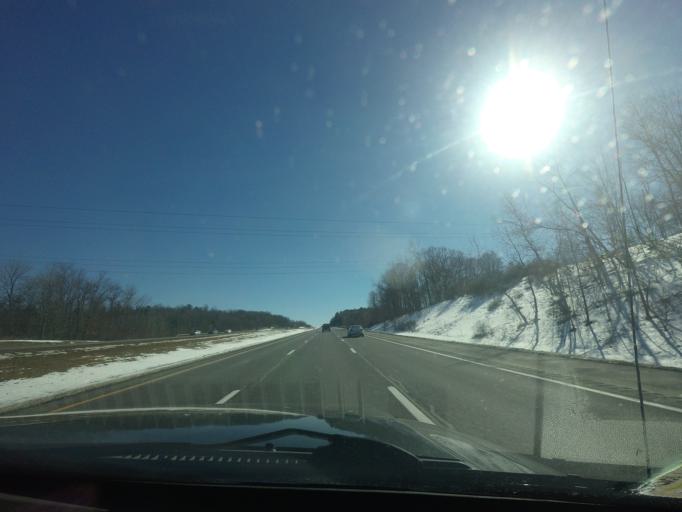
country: US
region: New York
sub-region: Rensselaer County
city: East Greenbush
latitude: 42.6167
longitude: -73.6899
